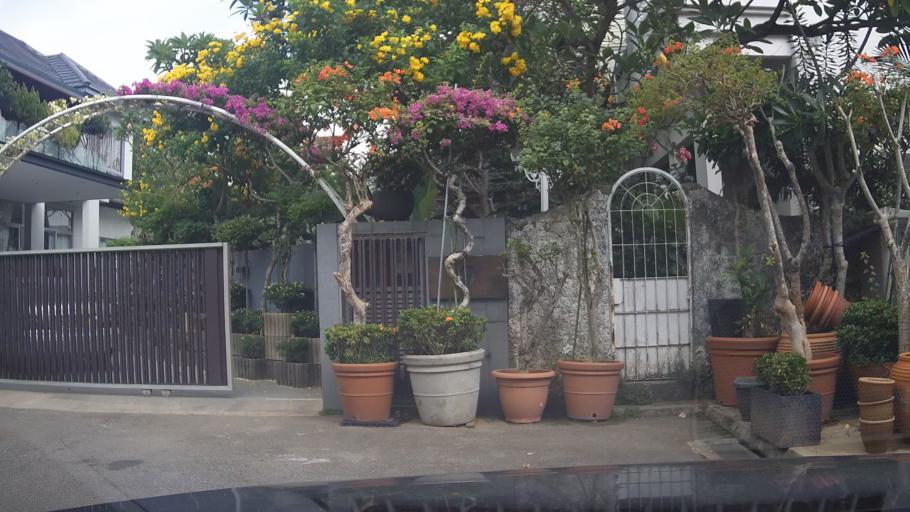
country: SG
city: Singapore
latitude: 1.2986
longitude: 103.8919
